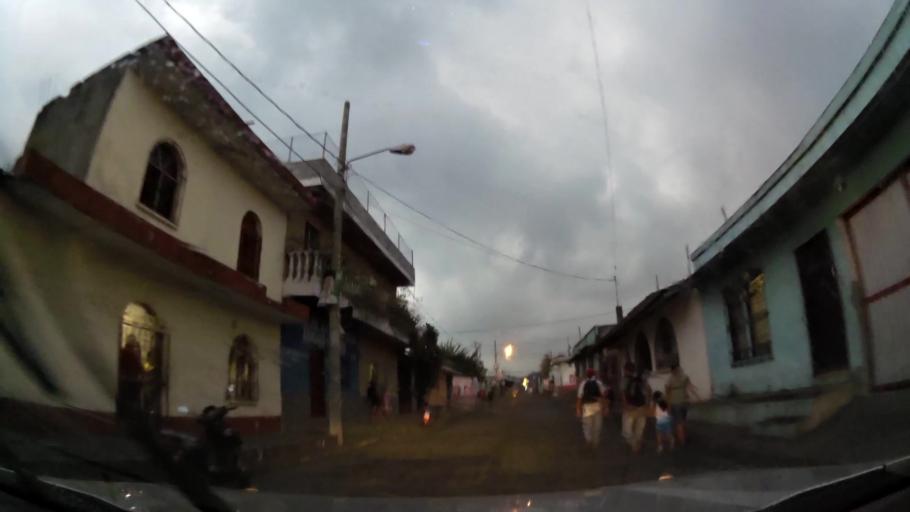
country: GT
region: Escuintla
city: Santa Lucia Cotzumalguapa
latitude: 14.3418
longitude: -91.0256
